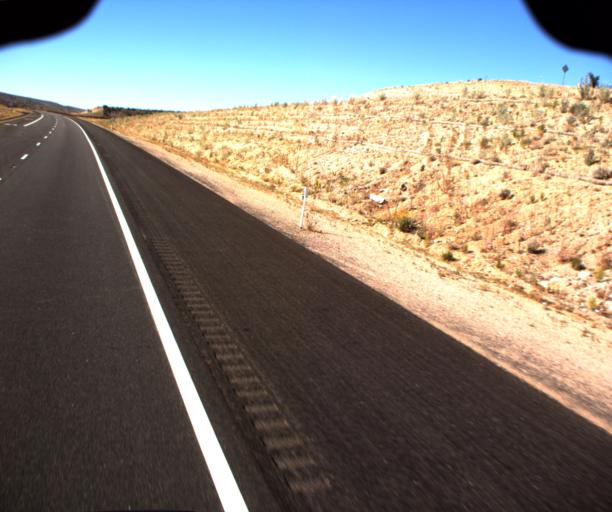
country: US
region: Arizona
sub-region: Mohave County
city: Kingman
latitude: 35.0067
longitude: -113.6648
